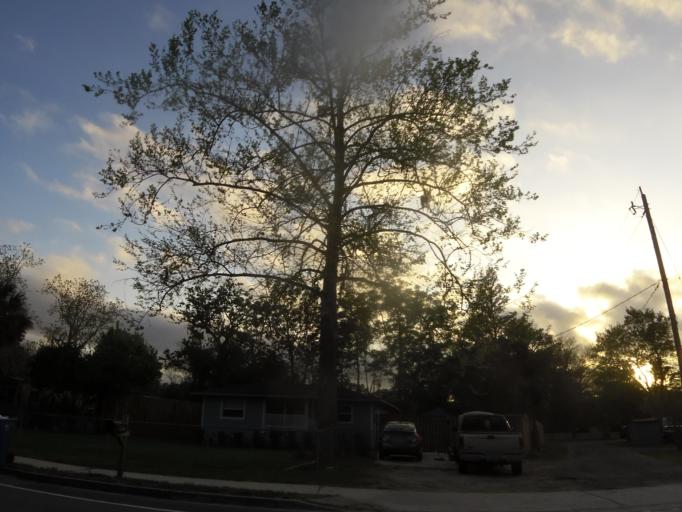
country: US
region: Florida
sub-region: Duval County
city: Jacksonville
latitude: 30.4592
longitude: -81.6137
